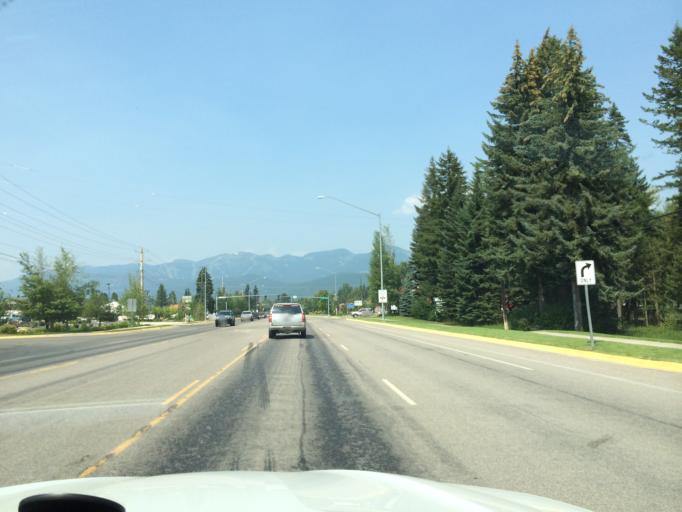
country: US
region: Montana
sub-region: Flathead County
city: Whitefish
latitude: 48.3982
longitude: -114.3353
